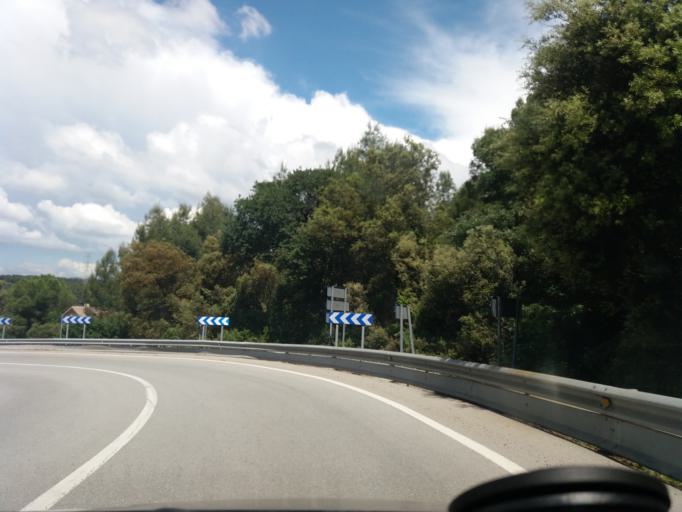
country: ES
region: Catalonia
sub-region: Provincia de Barcelona
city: Navarcles
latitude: 41.7645
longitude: 1.9093
